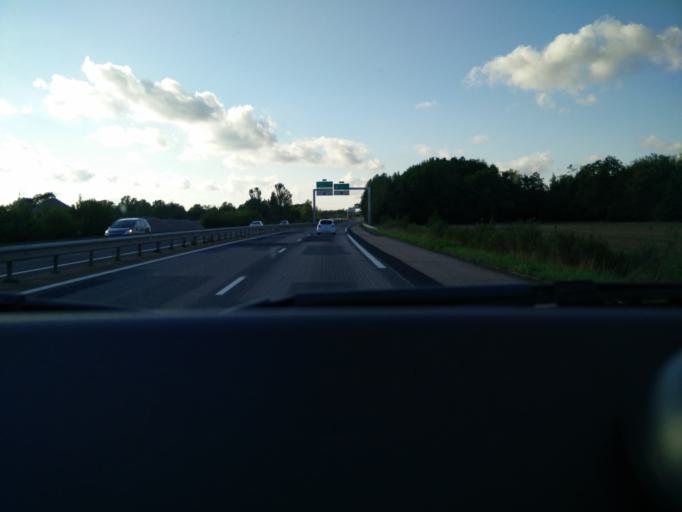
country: FR
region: Lorraine
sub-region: Departement de Meurthe-et-Moselle
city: Chanteheux
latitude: 48.5630
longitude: 6.5434
